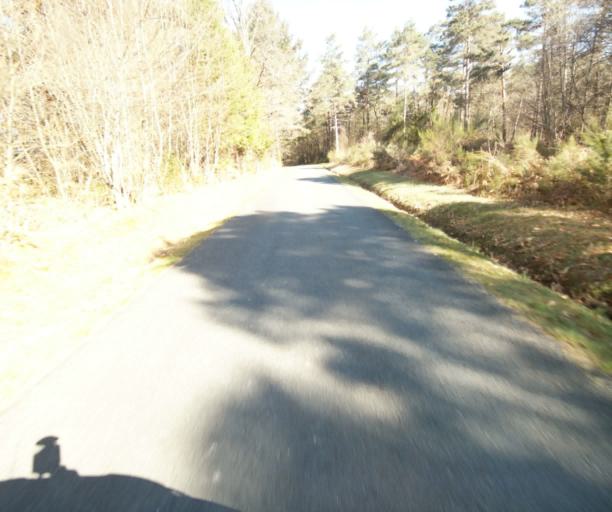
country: FR
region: Limousin
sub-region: Departement de la Correze
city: Correze
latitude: 45.2764
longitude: 1.9229
